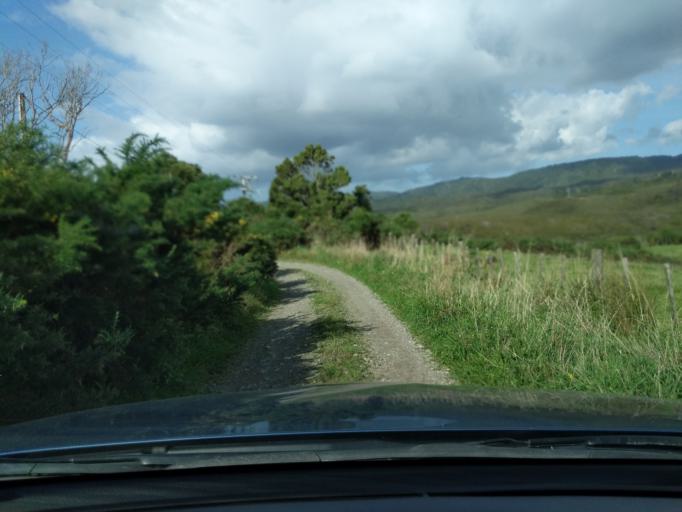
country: NZ
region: Tasman
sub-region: Tasman District
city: Takaka
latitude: -40.6512
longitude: 172.4763
